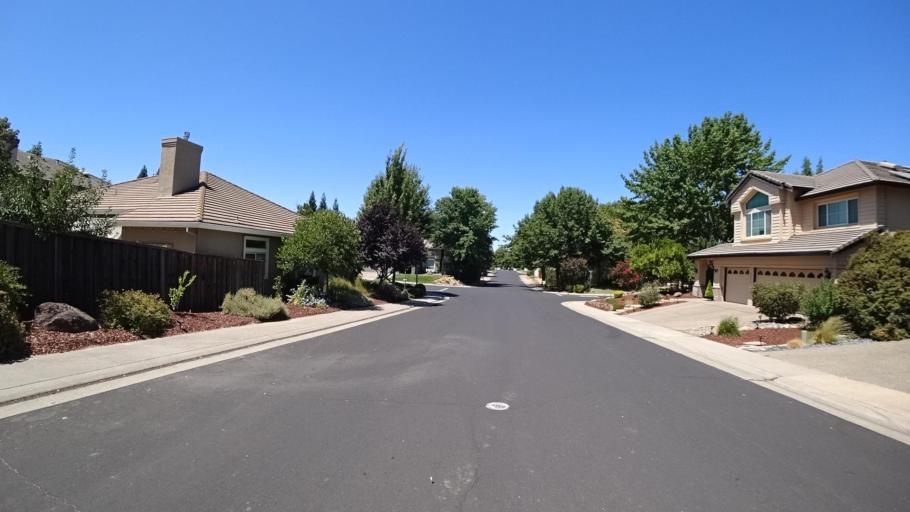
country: US
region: California
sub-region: Placer County
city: Rocklin
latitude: 38.8252
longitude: -121.2489
